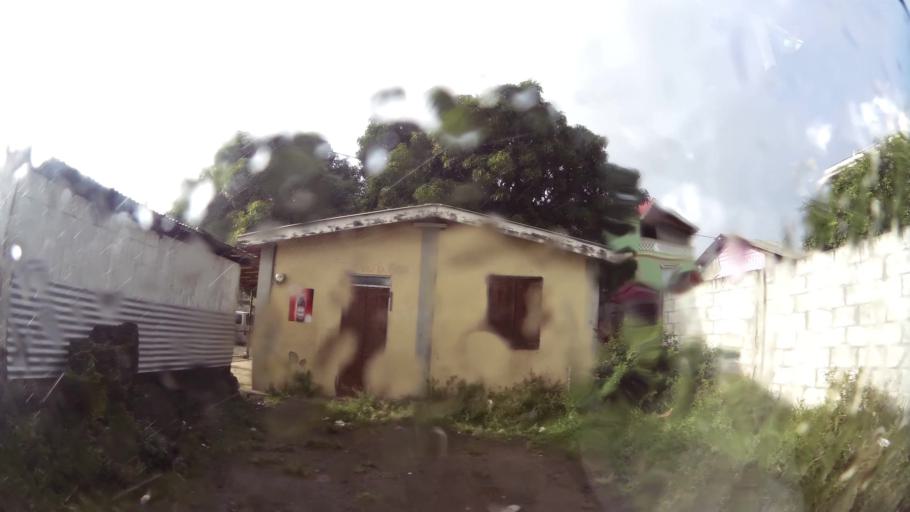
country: DM
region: Saint Paul
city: Mahaut
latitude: 15.3623
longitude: -61.3977
